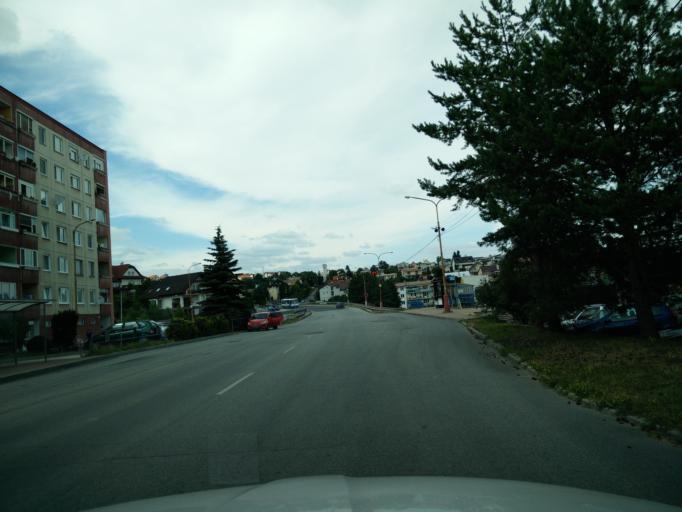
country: SK
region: Nitriansky
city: Bojnice
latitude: 48.8122
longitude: 18.5815
